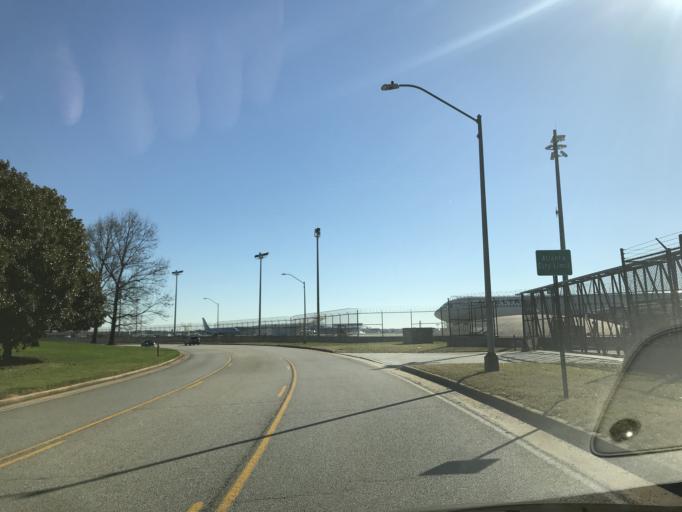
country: US
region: Georgia
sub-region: Fulton County
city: Hapeville
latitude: 33.6536
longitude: -84.4286
